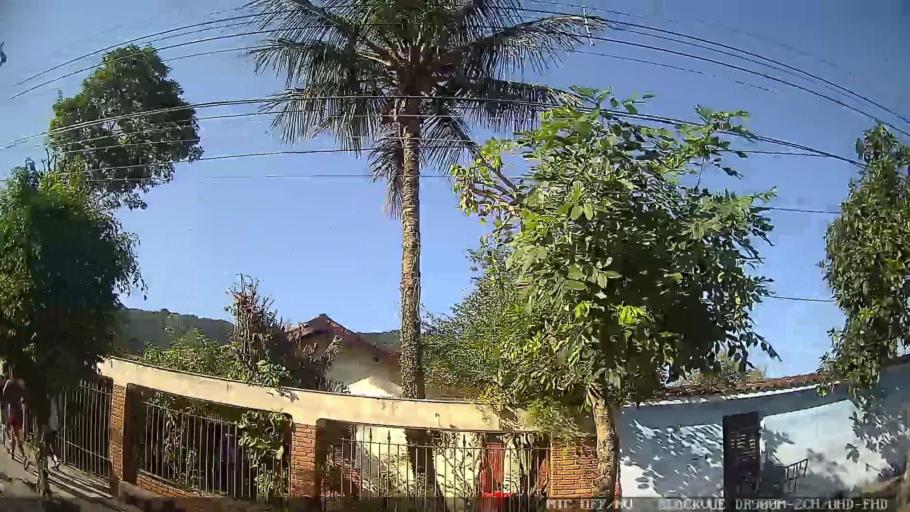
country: BR
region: Sao Paulo
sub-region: Guaruja
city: Guaruja
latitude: -24.0151
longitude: -46.2878
